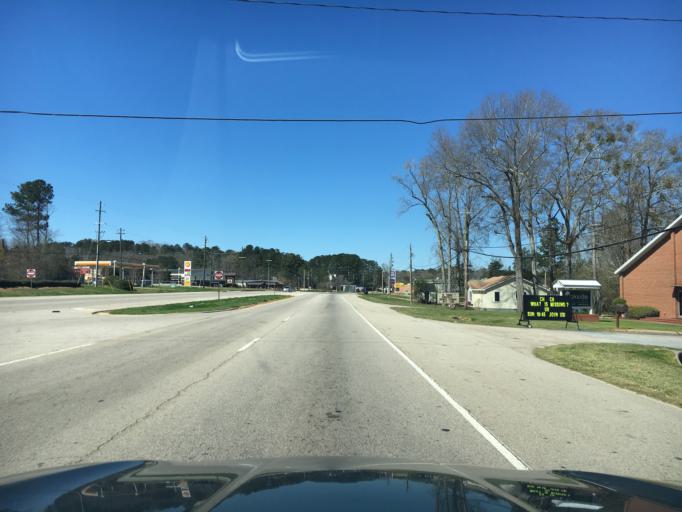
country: US
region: Georgia
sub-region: Troup County
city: La Grange
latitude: 33.0022
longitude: -85.0145
